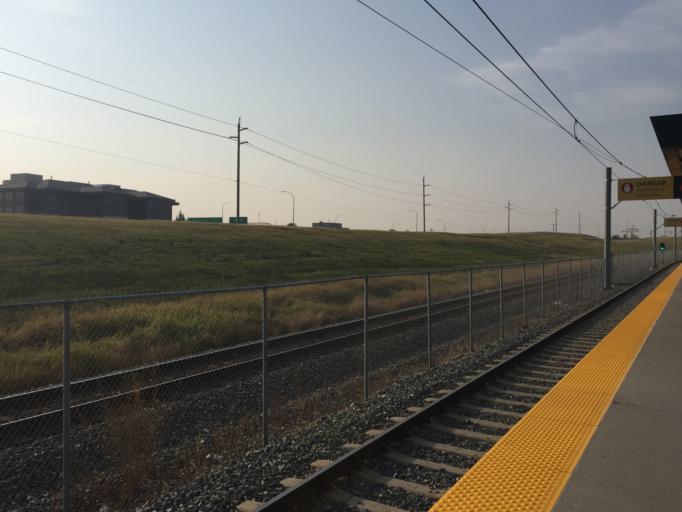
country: CA
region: Alberta
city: Calgary
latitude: 50.9358
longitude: -114.0698
